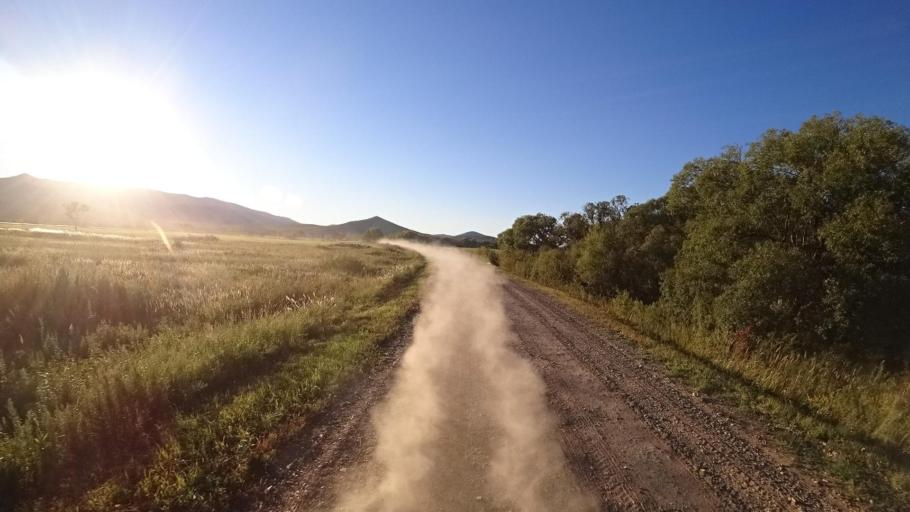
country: RU
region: Primorskiy
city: Kirovskiy
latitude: 44.8219
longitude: 133.6044
